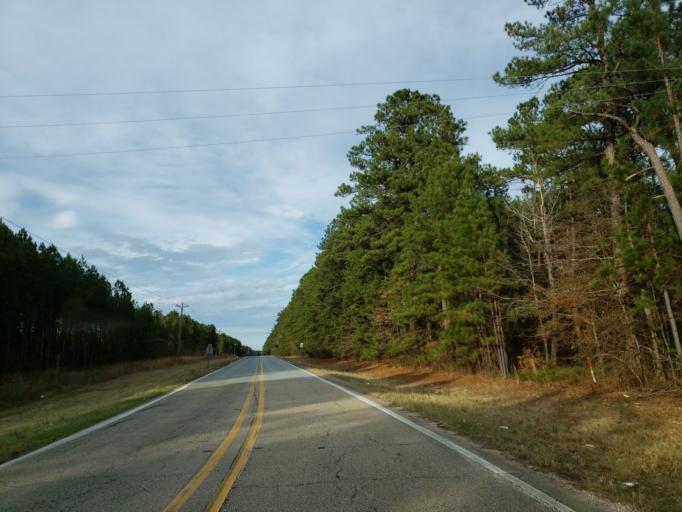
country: US
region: Mississippi
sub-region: Wayne County
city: Waynesboro
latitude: 31.8244
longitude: -88.6909
